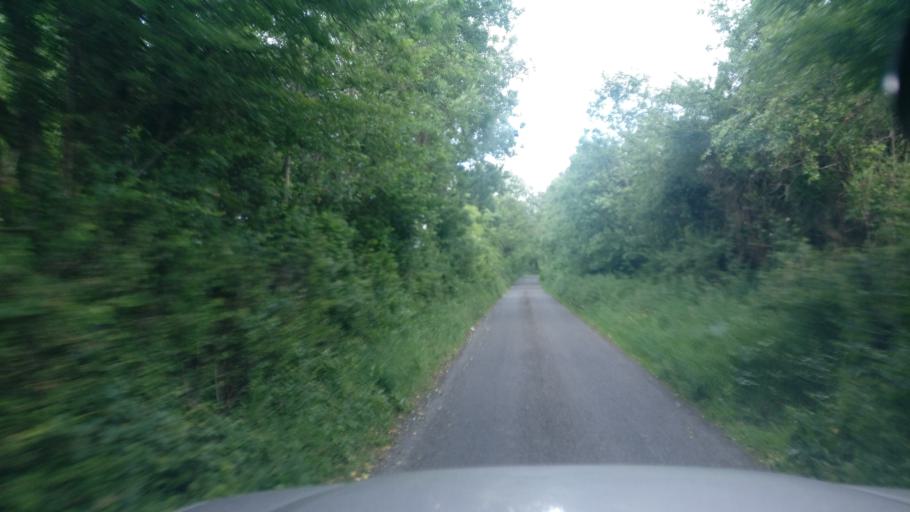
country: IE
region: Connaught
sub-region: County Galway
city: Portumna
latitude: 53.1999
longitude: -8.3382
